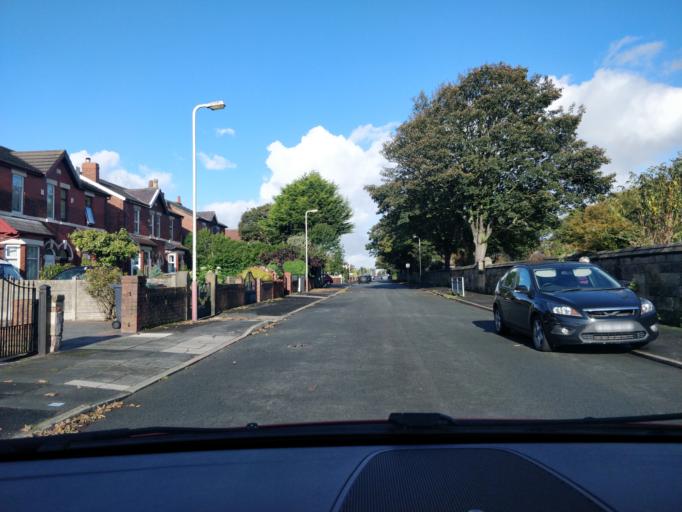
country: GB
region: England
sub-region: Sefton
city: Southport
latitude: 53.6330
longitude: -2.9978
